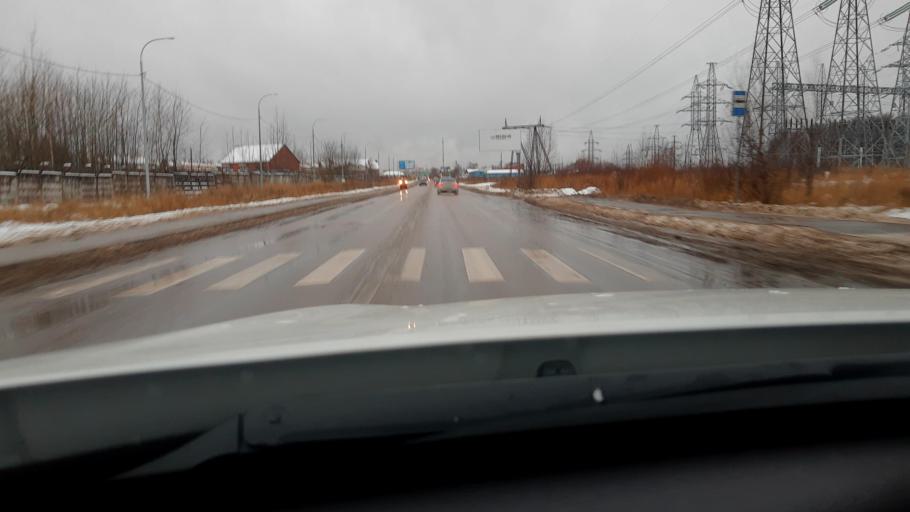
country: RU
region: Moskovskaya
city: Krasnogorsk
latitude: 55.8595
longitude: 37.3324
